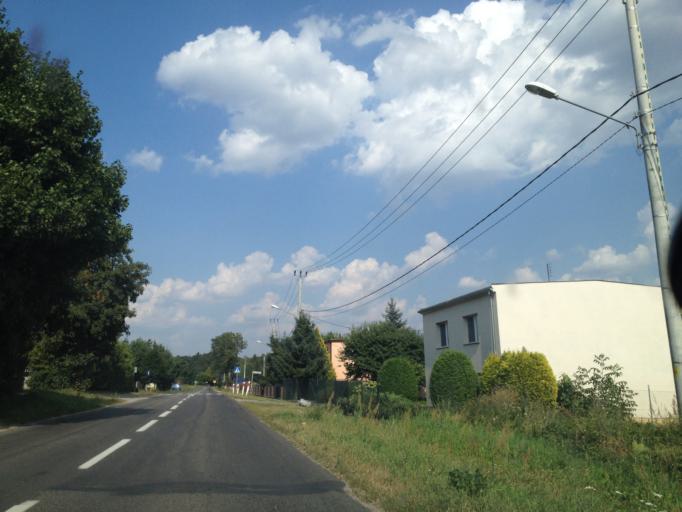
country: PL
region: Greater Poland Voivodeship
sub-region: Powiat poznanski
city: Daszewice
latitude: 52.2373
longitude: 17.0036
